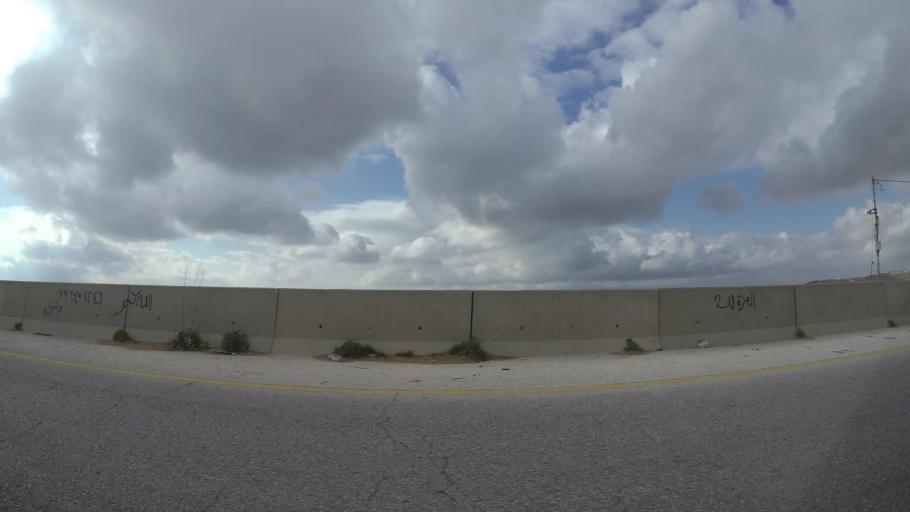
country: JO
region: Amman
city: Al Jubayhah
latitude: 32.0817
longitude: 35.8805
